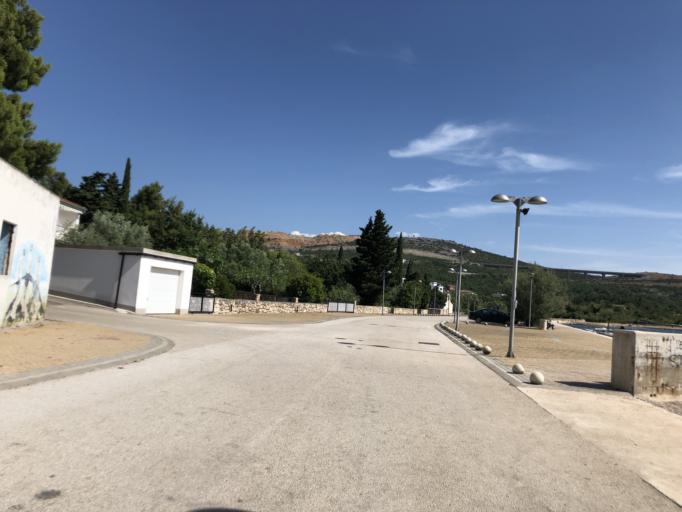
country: HR
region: Zadarska
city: Posedarje
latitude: 44.2502
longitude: 15.5374
